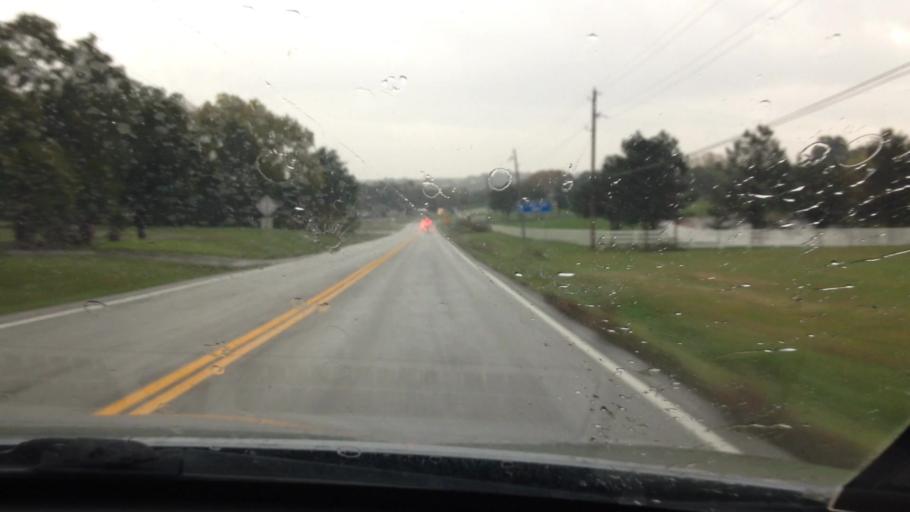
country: US
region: Missouri
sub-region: Platte County
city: Platte City
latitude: 39.3796
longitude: -94.8009
